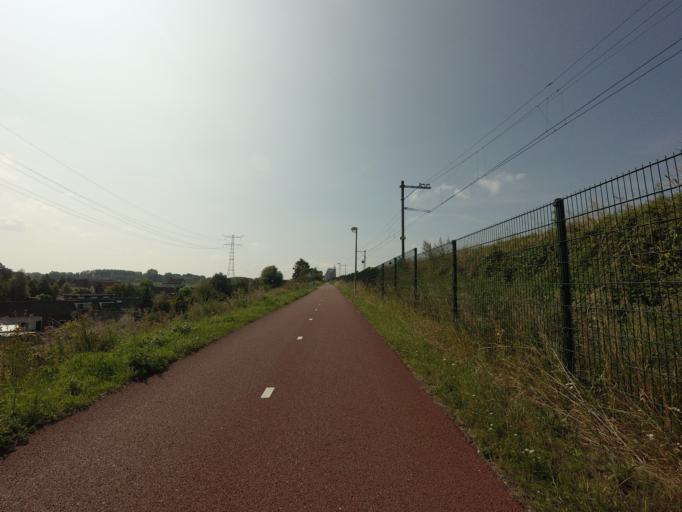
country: NL
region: South Holland
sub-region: Gemeente Sliedrecht
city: Sliedrecht
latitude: 51.8255
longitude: 4.7418
